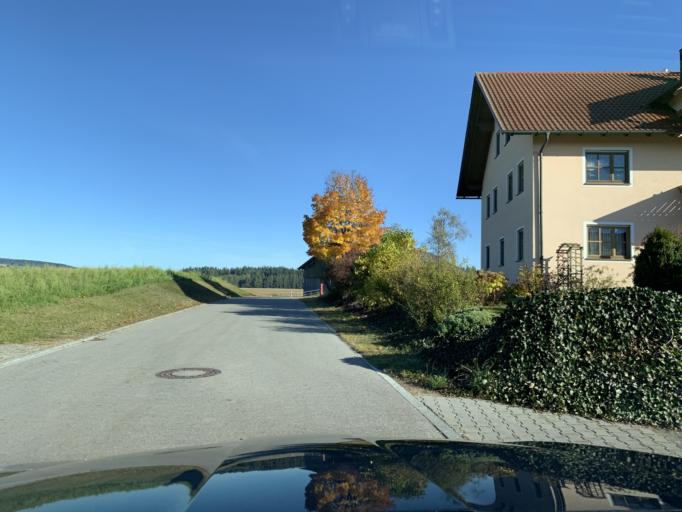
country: DE
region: Bavaria
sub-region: Upper Palatinate
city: Thanstein
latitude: 49.3848
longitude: 12.4807
